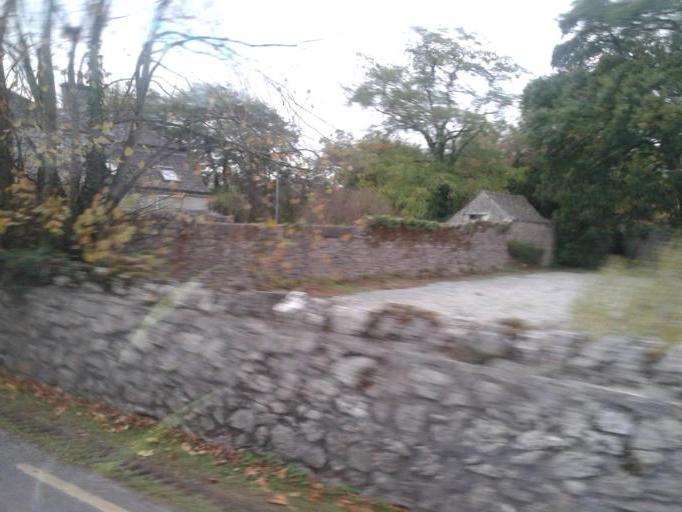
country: IE
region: Munster
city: Nenagh Bridge
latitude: 52.9442
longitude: -8.0350
